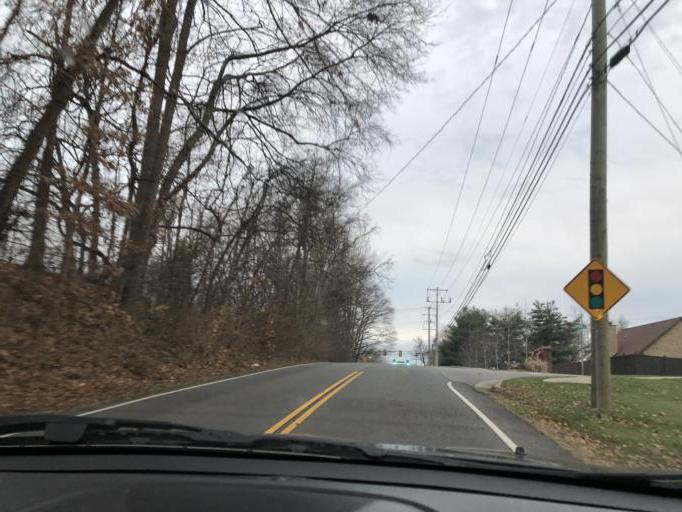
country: US
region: Tennessee
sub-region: Wilson County
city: Green Hill
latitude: 36.1903
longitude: -86.5931
